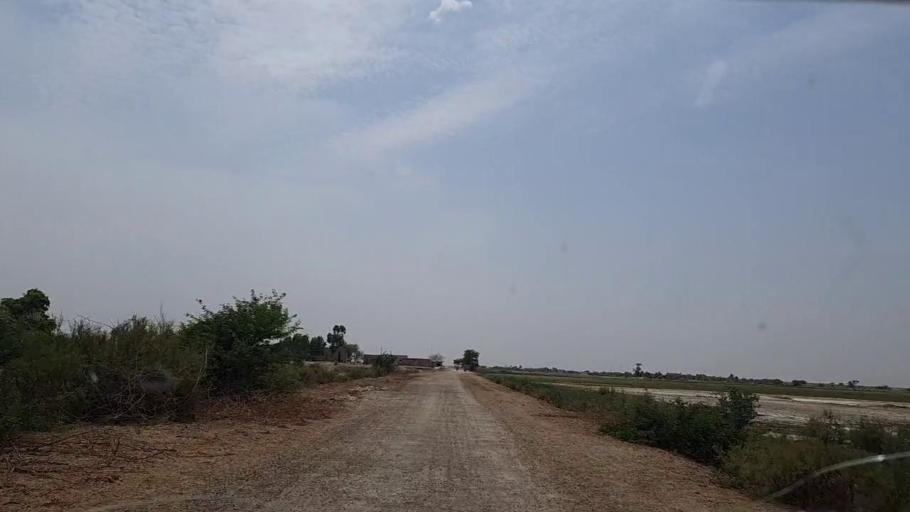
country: PK
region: Sindh
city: Phulji
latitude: 26.8794
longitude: 67.6671
